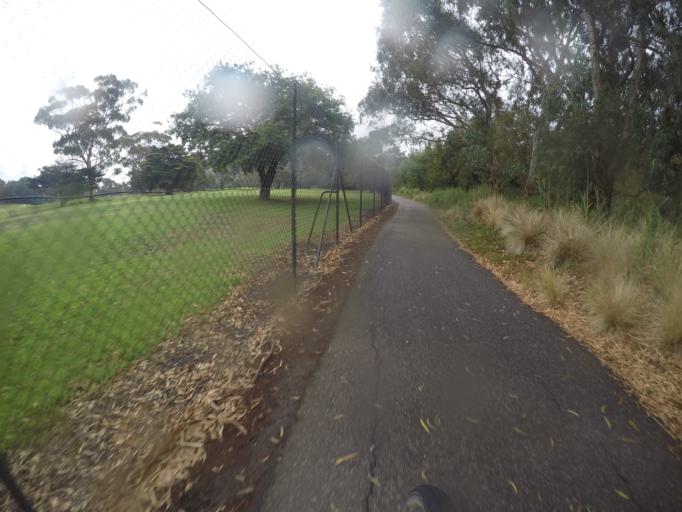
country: AU
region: Victoria
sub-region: Greater Geelong
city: Hamlyn Heights
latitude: -38.1467
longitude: 144.3223
